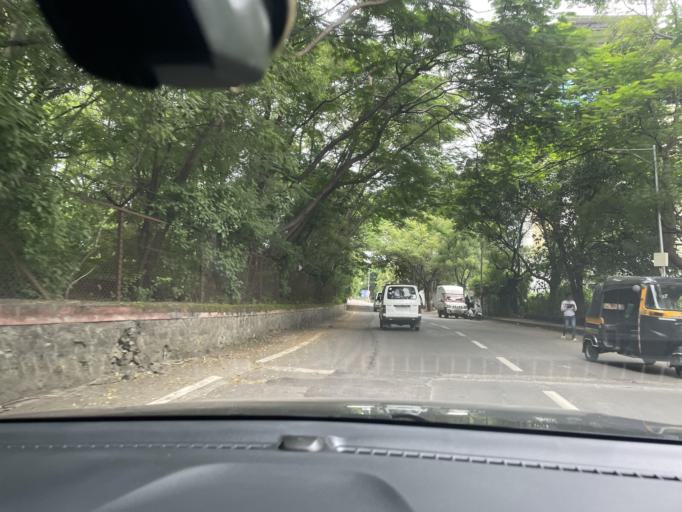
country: IN
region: Maharashtra
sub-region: Pune Division
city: Shivaji Nagar
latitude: 18.5359
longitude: 73.8111
